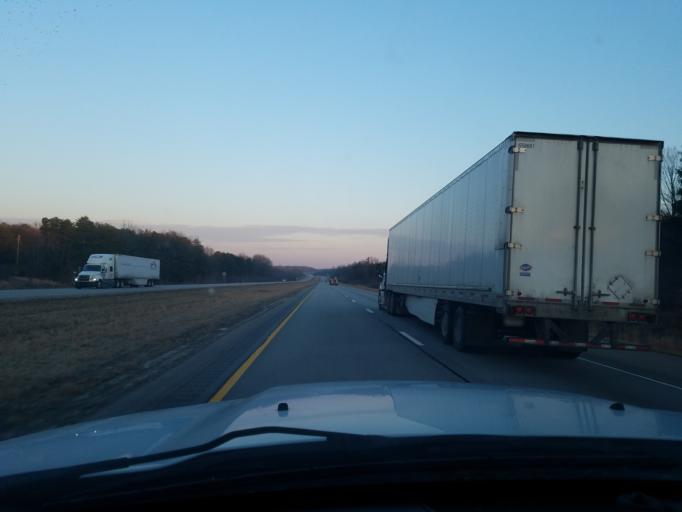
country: US
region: Indiana
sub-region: Gibson County
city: Oakland City
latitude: 38.1923
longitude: -87.3187
